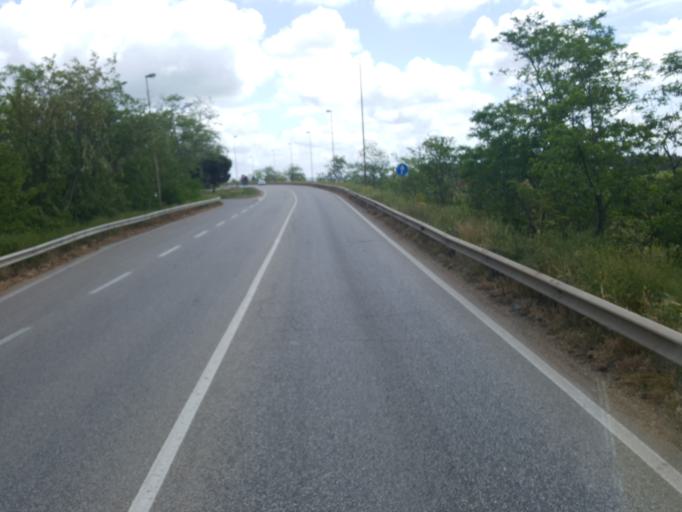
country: IT
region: Apulia
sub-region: Provincia di Bari
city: Altamura
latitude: 40.8151
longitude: 16.5544
